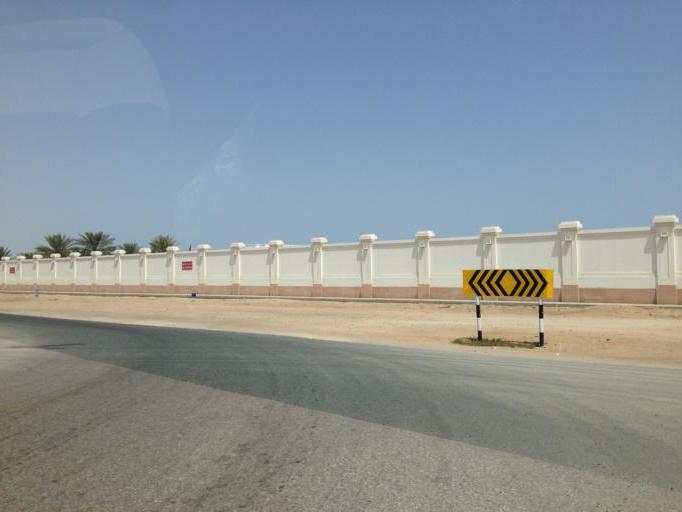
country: OM
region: Muhafazat Masqat
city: Bawshar
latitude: 23.6028
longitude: 58.3471
